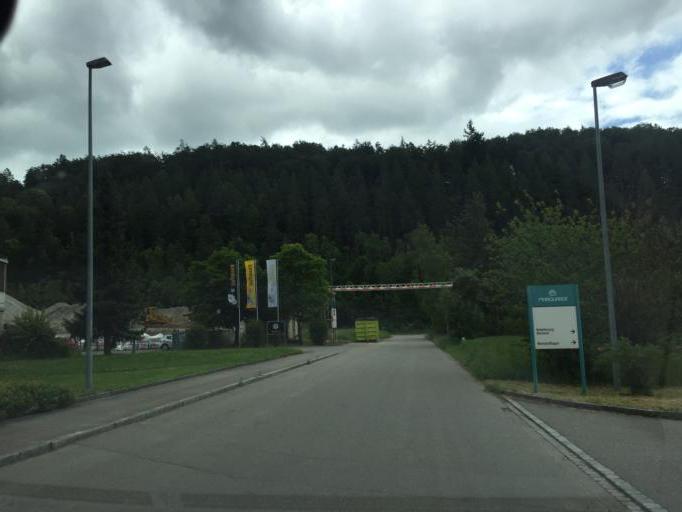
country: CH
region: Schaffhausen
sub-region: Bezirk Reiat
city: Stetten
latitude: 47.7185
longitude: 8.6692
